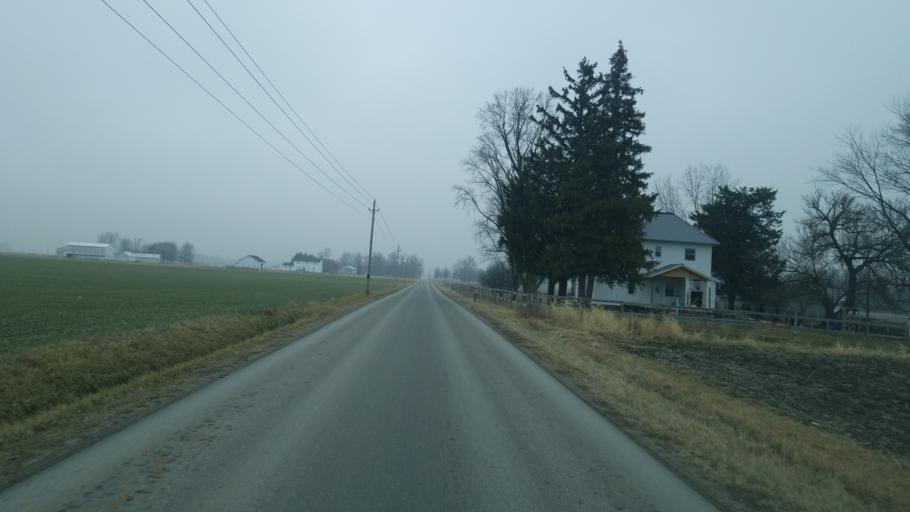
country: US
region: Indiana
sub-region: Adams County
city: Berne
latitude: 40.6798
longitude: -84.9943
